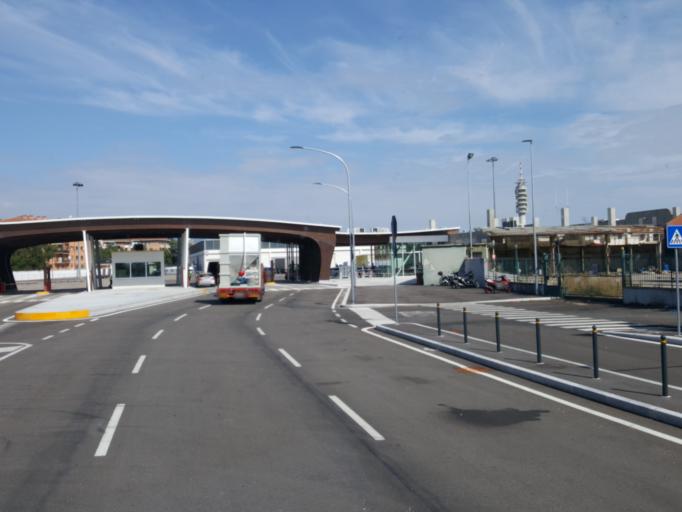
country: IT
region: Veneto
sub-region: Provincia di Verona
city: Verona
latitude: 45.4159
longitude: 10.9727
